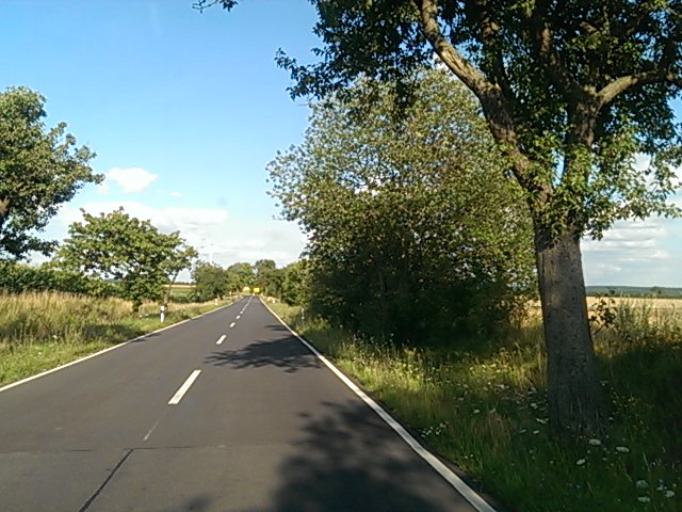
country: DE
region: Saxony-Anhalt
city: Nudersdorf
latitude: 51.9647
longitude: 12.5824
